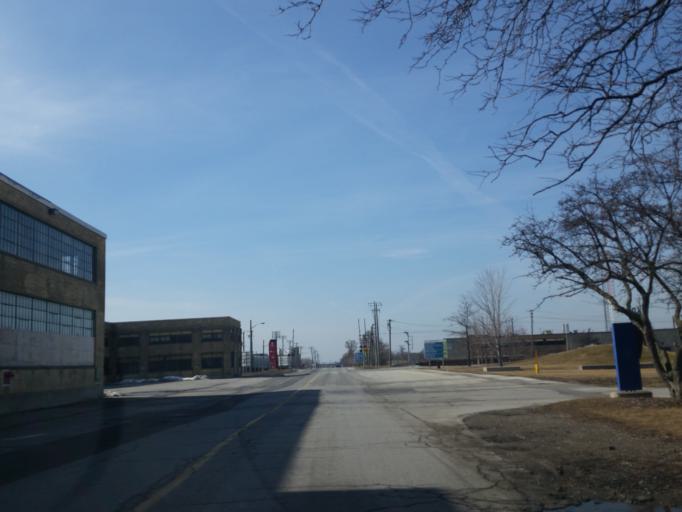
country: CA
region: Ontario
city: Concord
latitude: 43.7479
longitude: -79.4754
